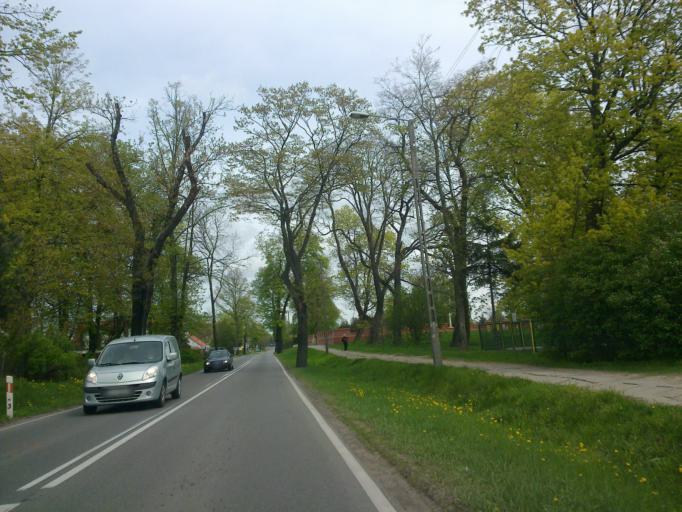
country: PL
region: Pomeranian Voivodeship
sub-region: Powiat malborski
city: Malbork
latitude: 54.0208
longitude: 19.0133
